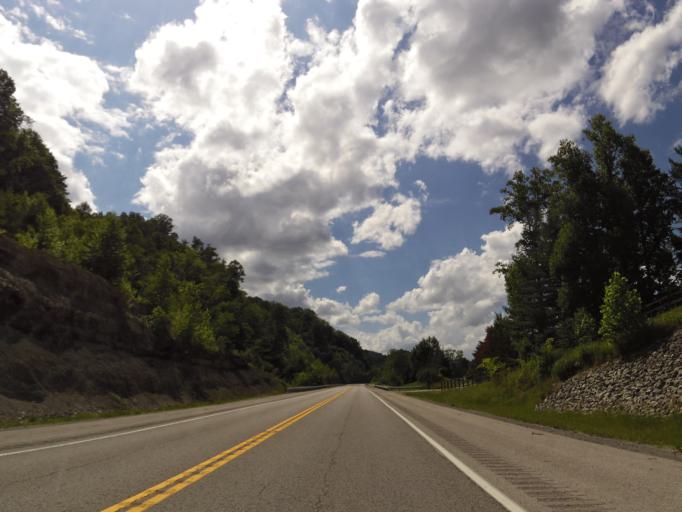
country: US
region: Kentucky
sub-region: Harlan County
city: Harlan
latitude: 36.7831
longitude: -83.2412
